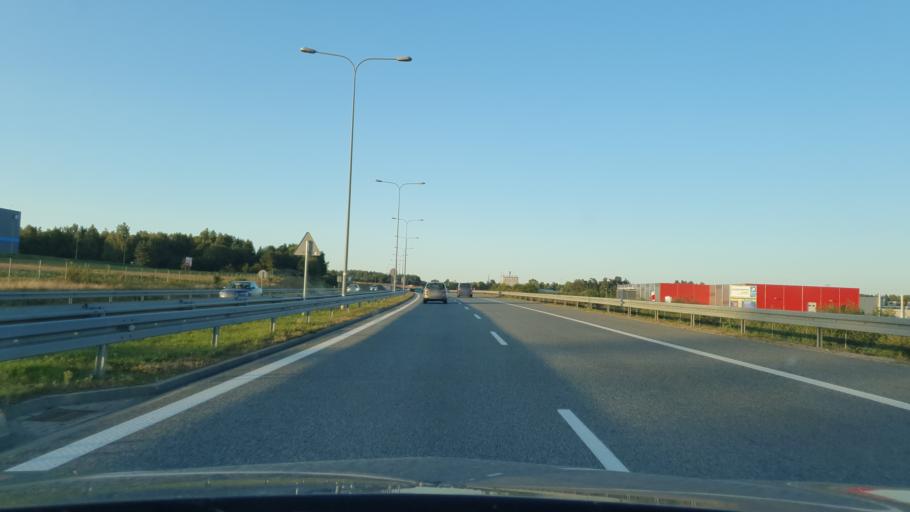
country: PL
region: Pomeranian Voivodeship
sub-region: Slupsk
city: Slupsk
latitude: 54.4454
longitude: 17.0792
